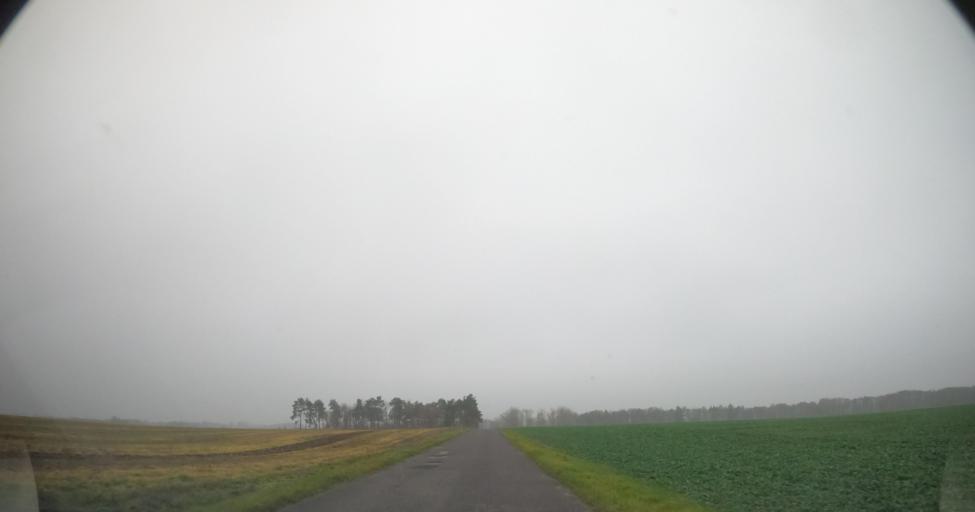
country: PL
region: West Pomeranian Voivodeship
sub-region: Powiat drawski
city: Drawsko Pomorskie
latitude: 53.6058
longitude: 15.7396
